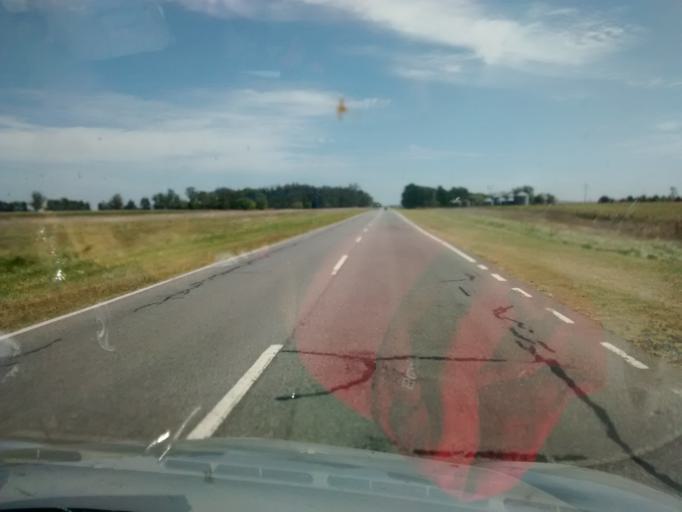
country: AR
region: Buenos Aires
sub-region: Partido de Balcarce
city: Balcarce
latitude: -37.6695
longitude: -58.5285
